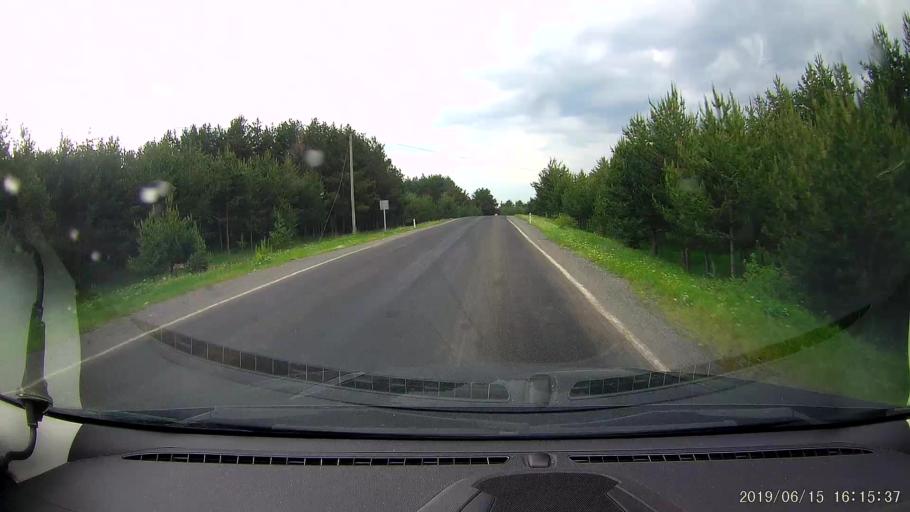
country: TR
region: Ardahan
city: Hanak
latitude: 41.2662
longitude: 42.8563
